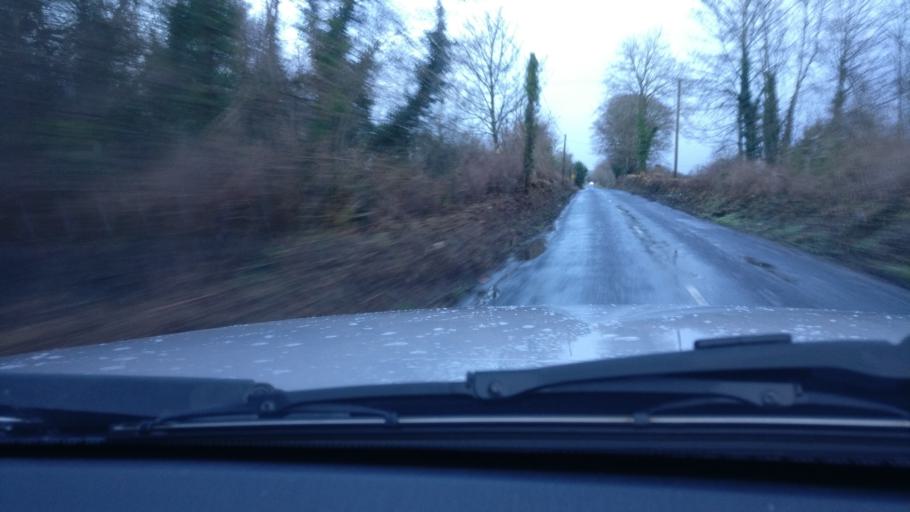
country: IE
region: Connaught
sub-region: County Galway
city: Ballinasloe
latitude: 53.2231
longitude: -8.3647
